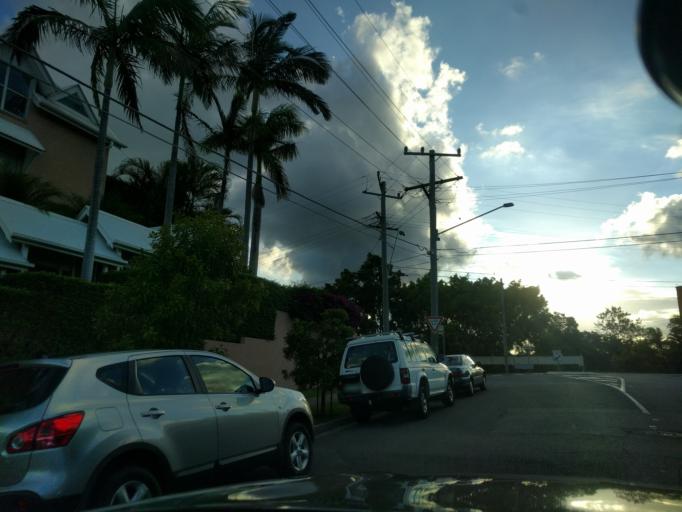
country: AU
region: Queensland
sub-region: Brisbane
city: Milton
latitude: -27.4639
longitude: 153.0006
